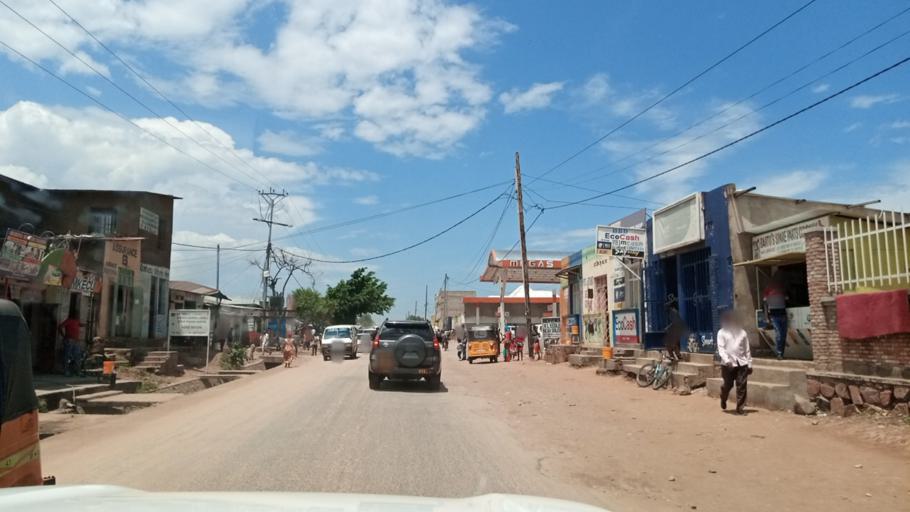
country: BI
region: Bujumbura Mairie
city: Bujumbura
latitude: -3.4257
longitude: 29.3556
